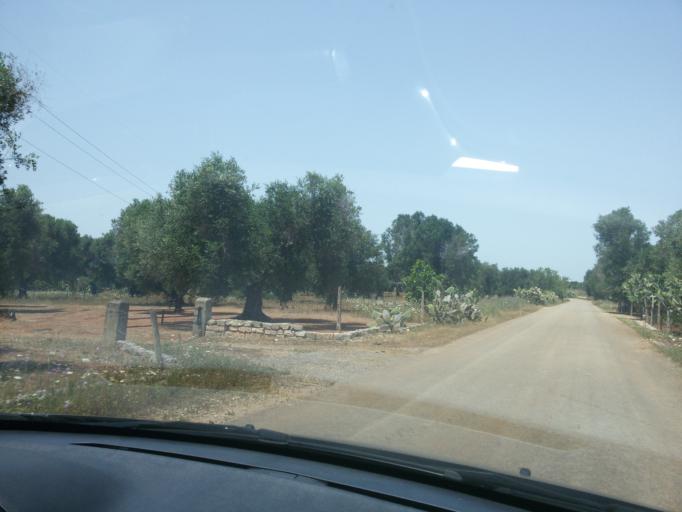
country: IT
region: Apulia
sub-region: Provincia di Lecce
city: Porto Cesareo
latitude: 40.3223
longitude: 17.8931
